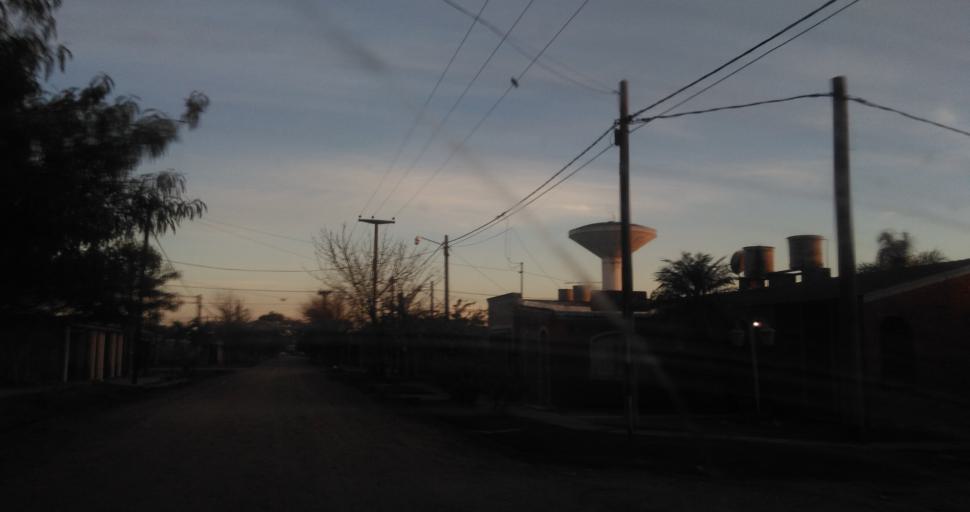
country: AR
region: Chaco
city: Resistencia
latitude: -27.4650
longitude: -59.0061
